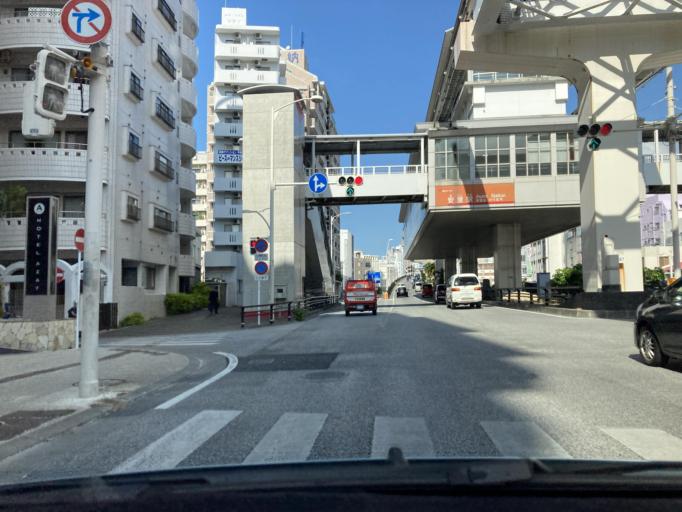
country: JP
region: Okinawa
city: Naha-shi
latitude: 26.2164
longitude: 127.6954
